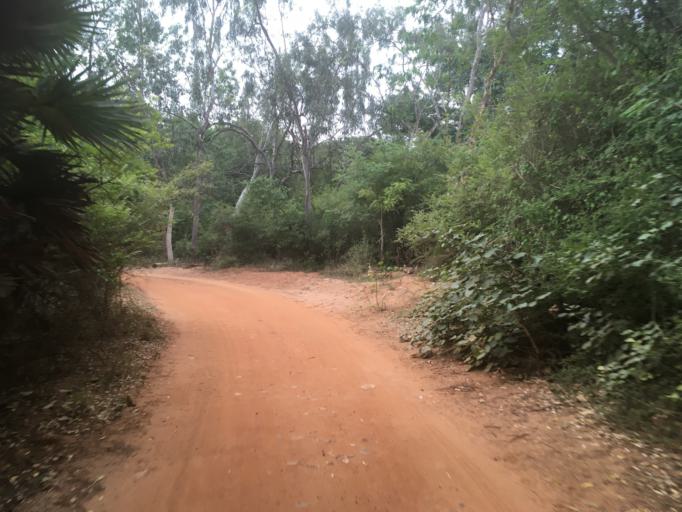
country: IN
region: Tamil Nadu
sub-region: Villupuram
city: Auroville
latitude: 12.0143
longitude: 79.8045
